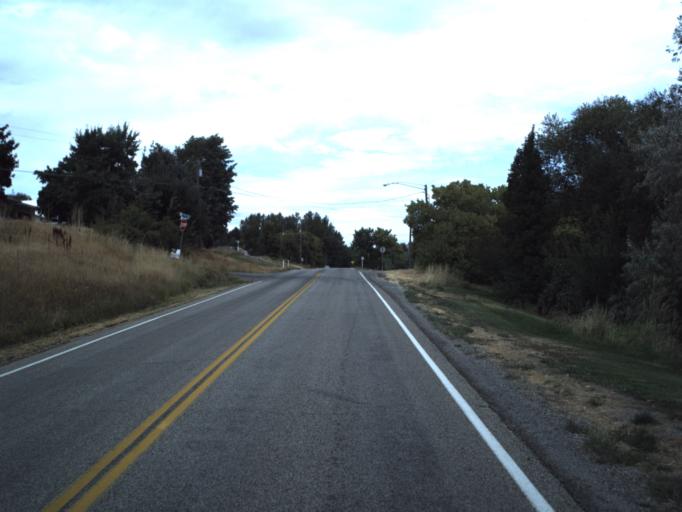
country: US
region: Utah
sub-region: Cache County
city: Mendon
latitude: 41.6998
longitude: -111.9764
